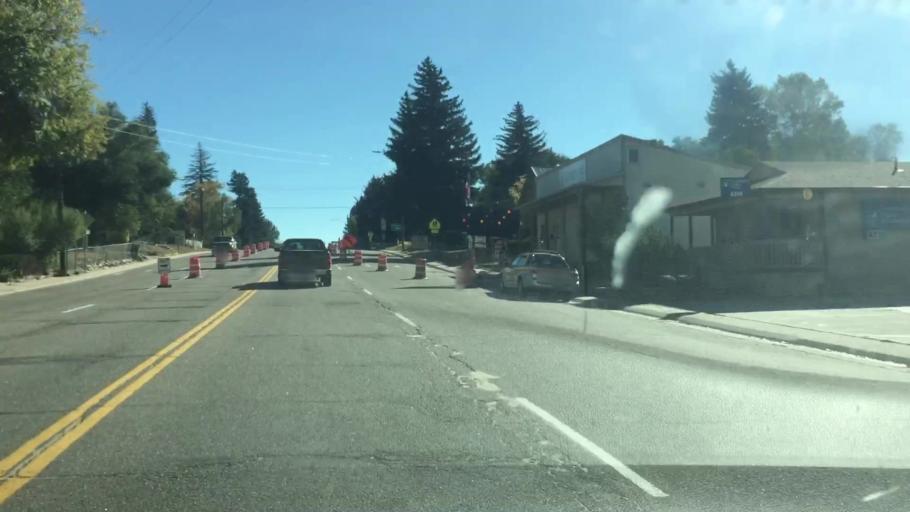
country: US
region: Colorado
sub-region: Elbert County
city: Kiowa
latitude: 39.3466
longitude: -104.4653
